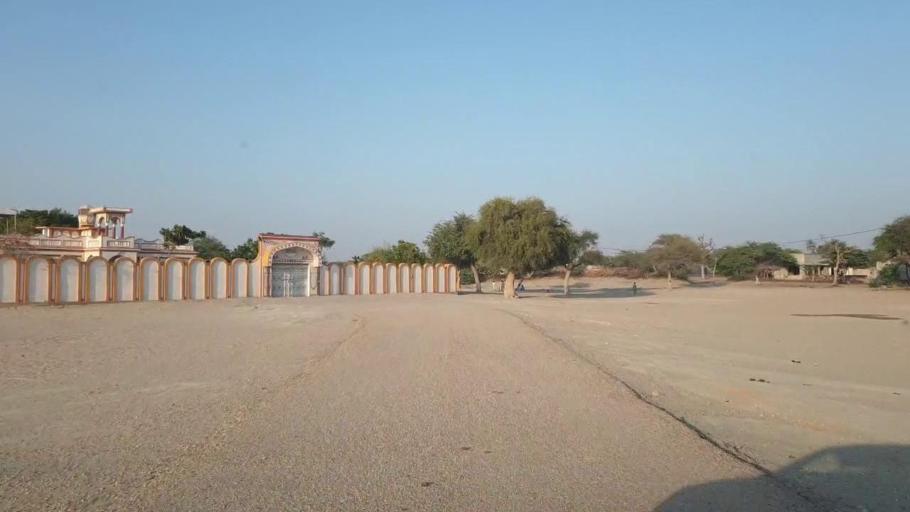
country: PK
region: Sindh
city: Chor
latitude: 25.5396
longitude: 69.8030
